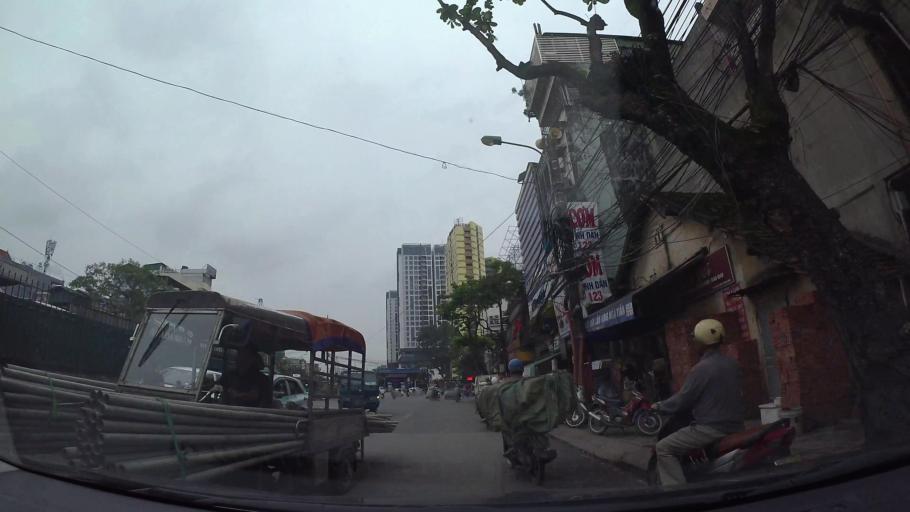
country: VN
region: Ha Noi
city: Hai BaTrung
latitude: 21.0140
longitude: 105.8628
